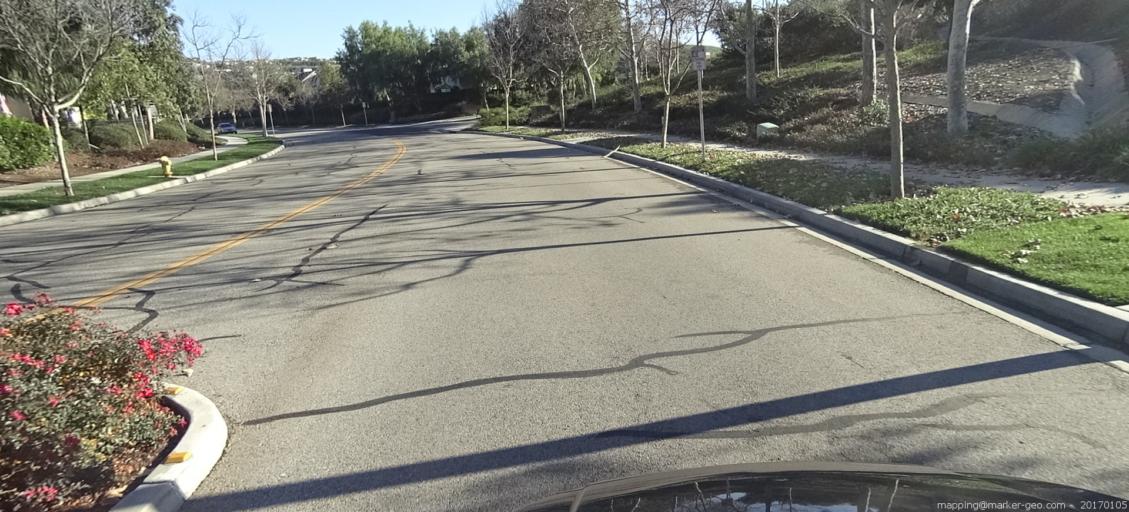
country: US
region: California
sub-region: Orange County
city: Ladera Ranch
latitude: 33.5386
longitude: -117.6475
